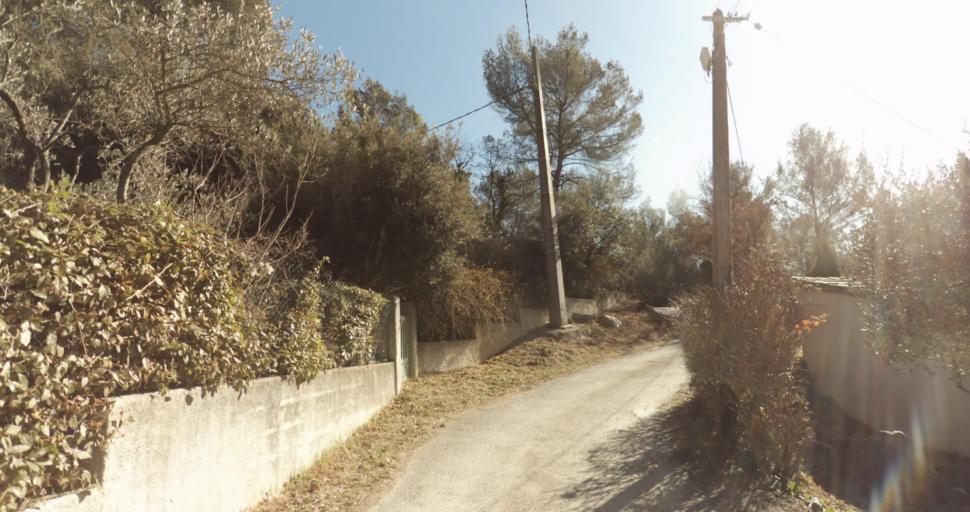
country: FR
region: Provence-Alpes-Cote d'Azur
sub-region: Departement des Bouches-du-Rhone
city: Peypin
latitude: 43.3862
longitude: 5.5836
